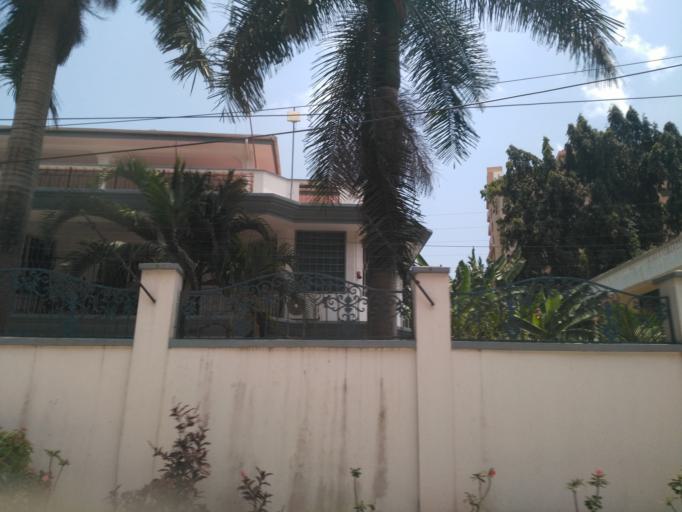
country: TZ
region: Dar es Salaam
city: Dar es Salaam
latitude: -6.8018
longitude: 39.2749
